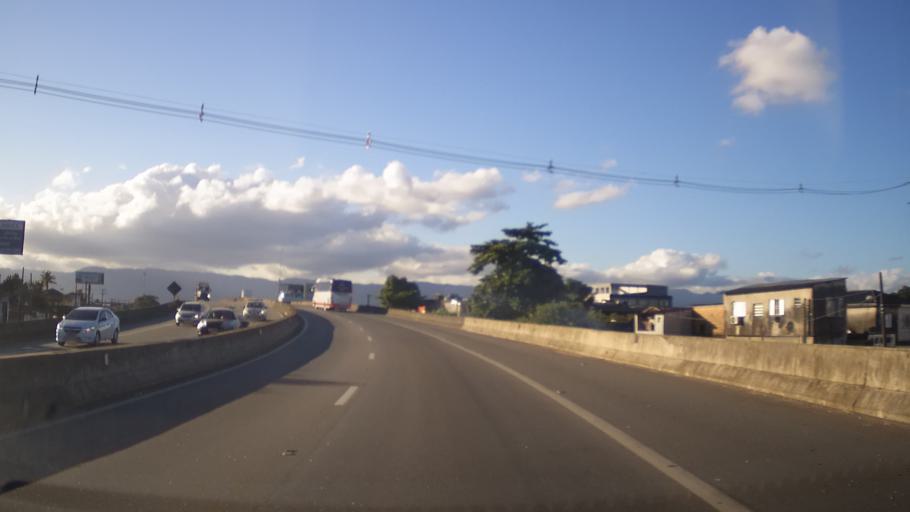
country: BR
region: Sao Paulo
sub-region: Sao Vicente
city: Sao Vicente
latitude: -23.9668
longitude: -46.4002
